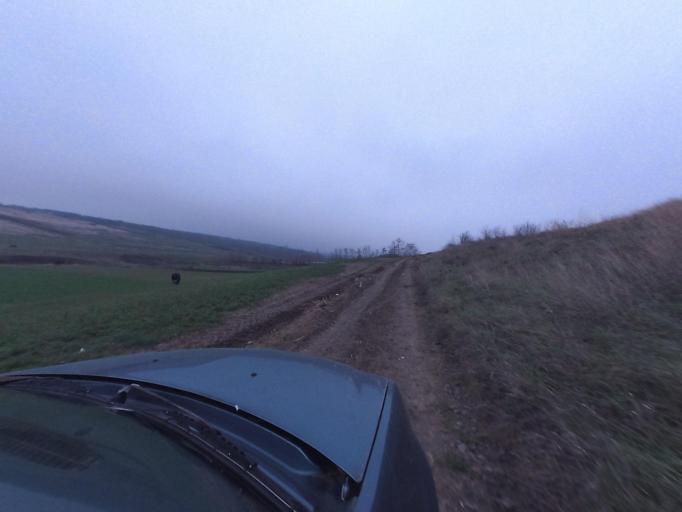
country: RO
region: Galati
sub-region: Comuna Balabanesti
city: Balabanesti
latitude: 46.1339
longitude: 27.7500
